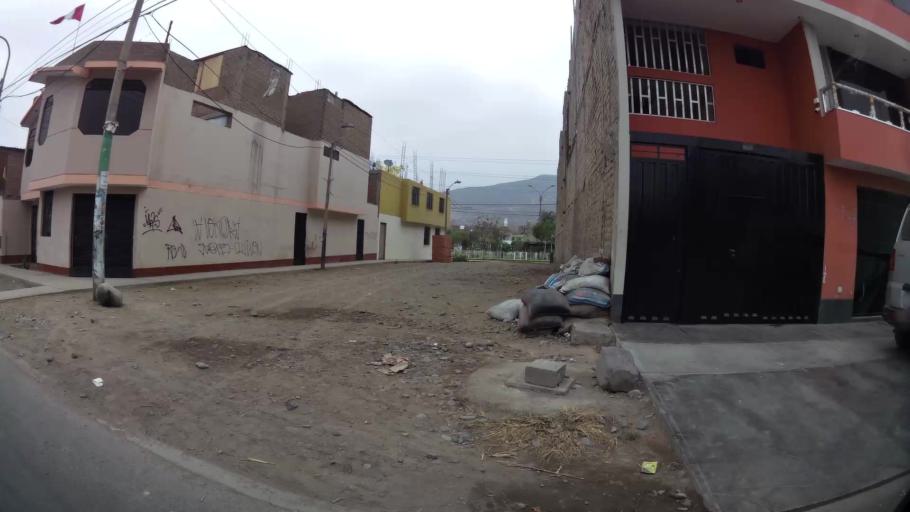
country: PE
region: Lima
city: Ventanilla
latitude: -11.9252
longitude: -77.0774
